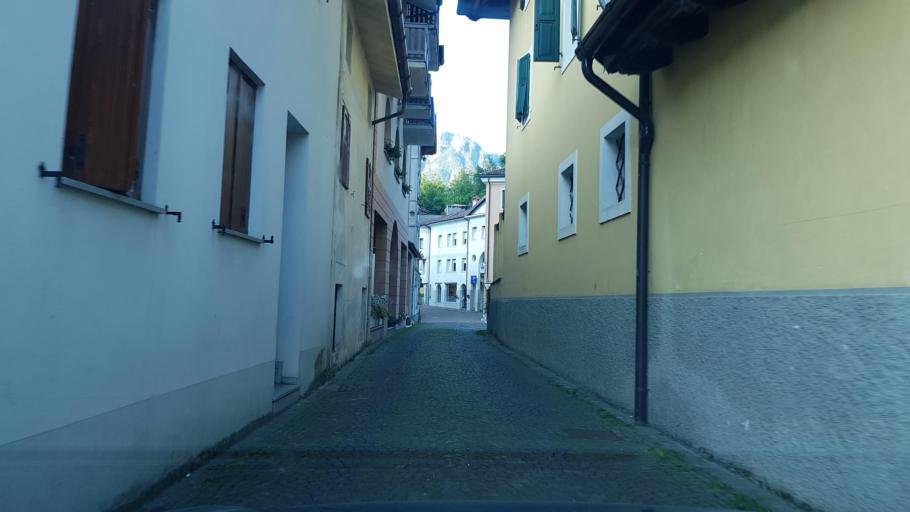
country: IT
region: Friuli Venezia Giulia
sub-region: Provincia di Udine
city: Moggio di Sotto
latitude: 46.4109
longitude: 13.1953
